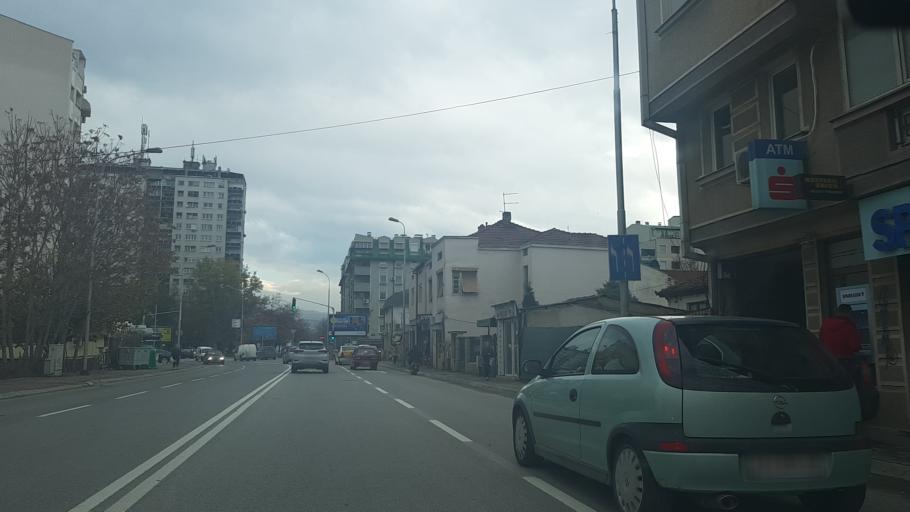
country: MK
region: Karpos
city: Skopje
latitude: 41.9821
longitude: 21.4401
